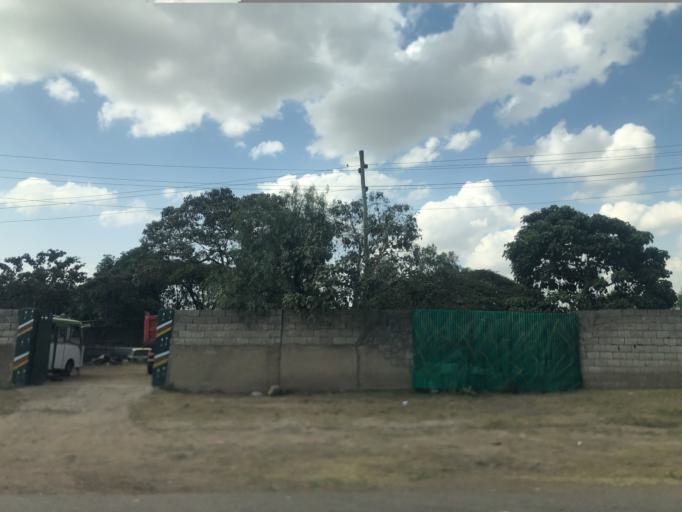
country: ET
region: Southern Nations, Nationalities, and People's Region
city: K'olito
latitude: 7.3018
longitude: 38.0858
